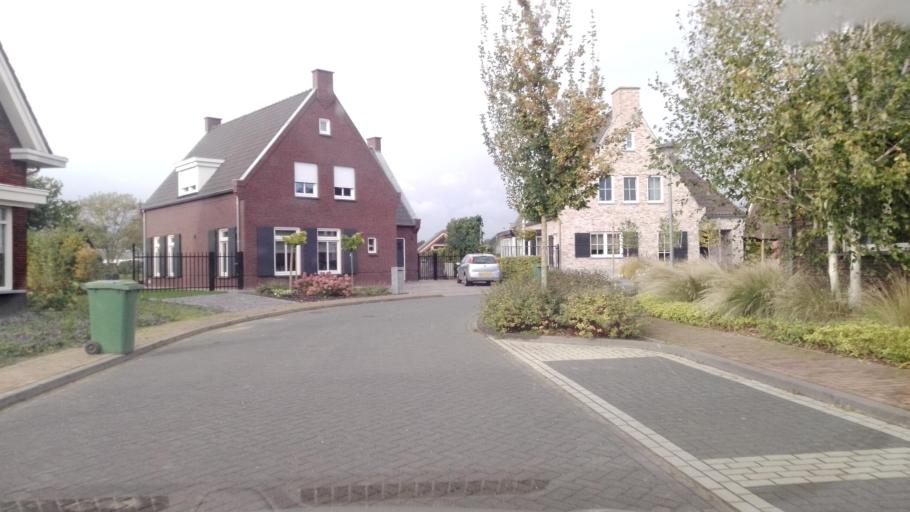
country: NL
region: Limburg
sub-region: Gemeente Venlo
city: Venlo
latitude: 51.4150
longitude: 6.1758
